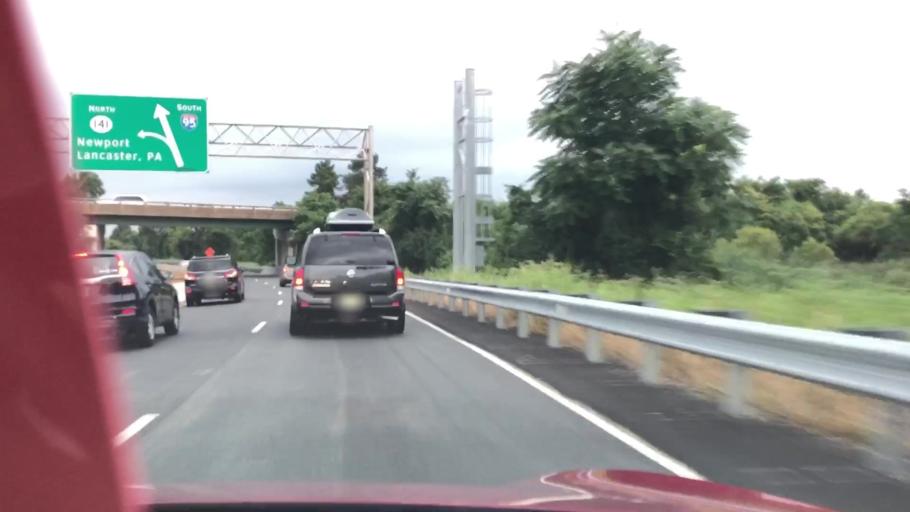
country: US
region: Delaware
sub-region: New Castle County
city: Newport
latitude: 39.7062
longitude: -75.5910
